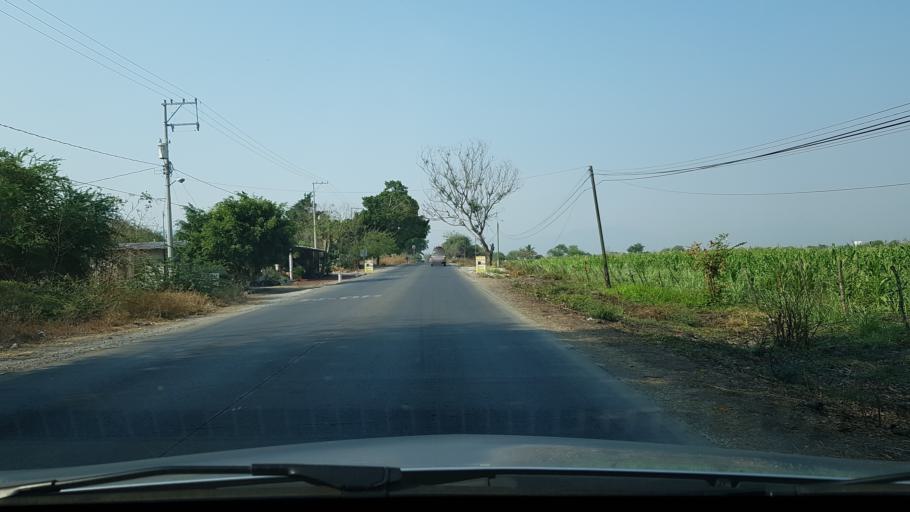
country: MX
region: Morelos
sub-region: Tlaquiltenango
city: Alfredo V. Bonfil (Chacampalco)
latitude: 18.6687
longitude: -99.1465
